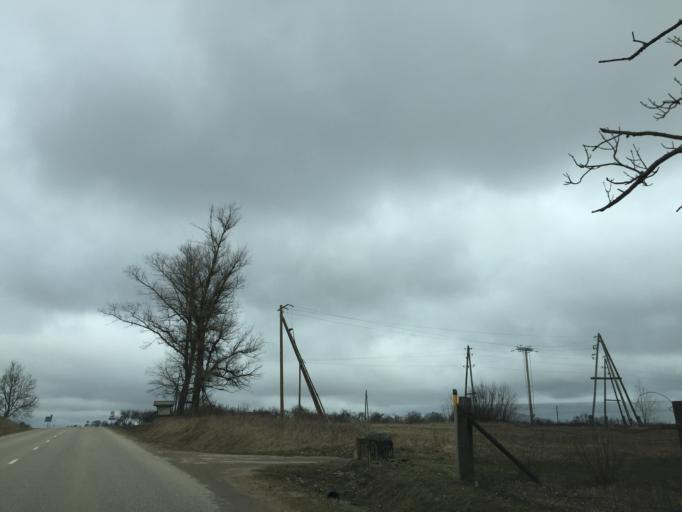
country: LV
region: Ilukste
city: Ilukste
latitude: 55.9855
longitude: 26.2896
